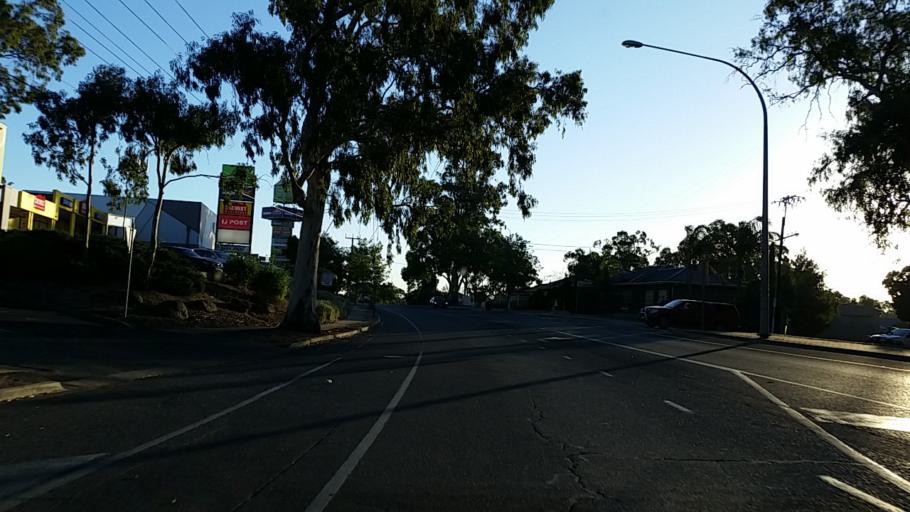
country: AU
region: South Australia
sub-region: Campbelltown
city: Athelstone
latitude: -34.8705
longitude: 138.7015
